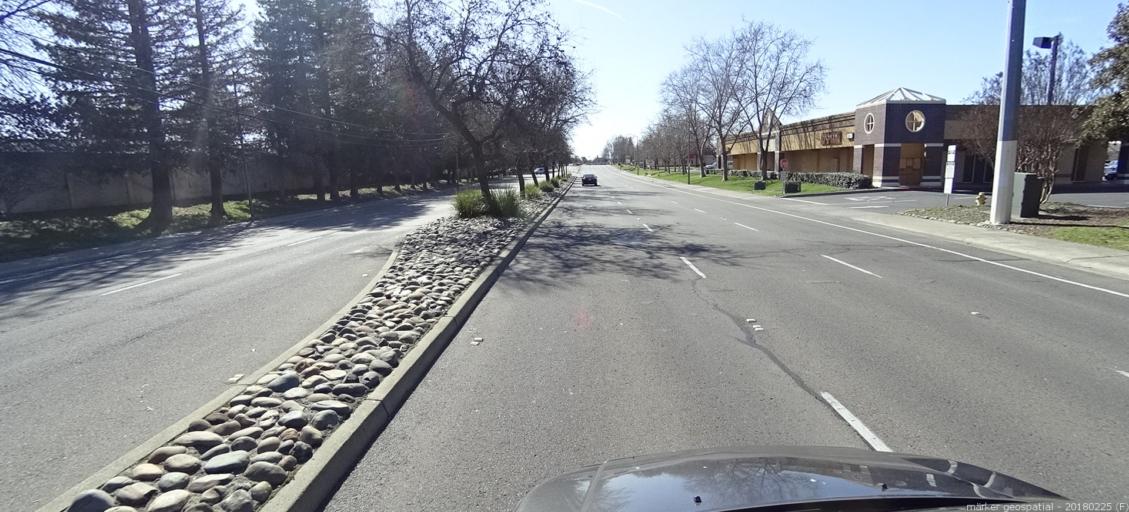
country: US
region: California
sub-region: Sacramento County
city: North Highlands
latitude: 38.7182
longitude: -121.3925
